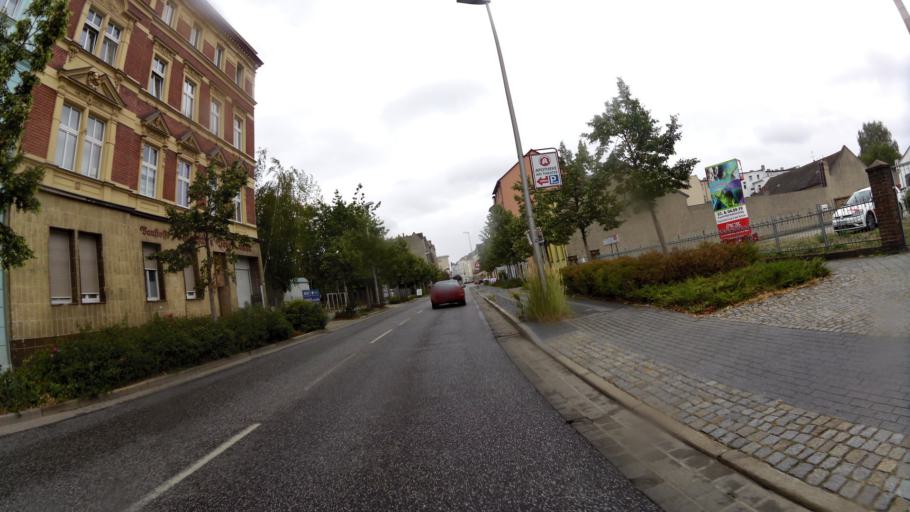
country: DE
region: Brandenburg
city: Cottbus
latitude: 51.7541
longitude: 14.3252
